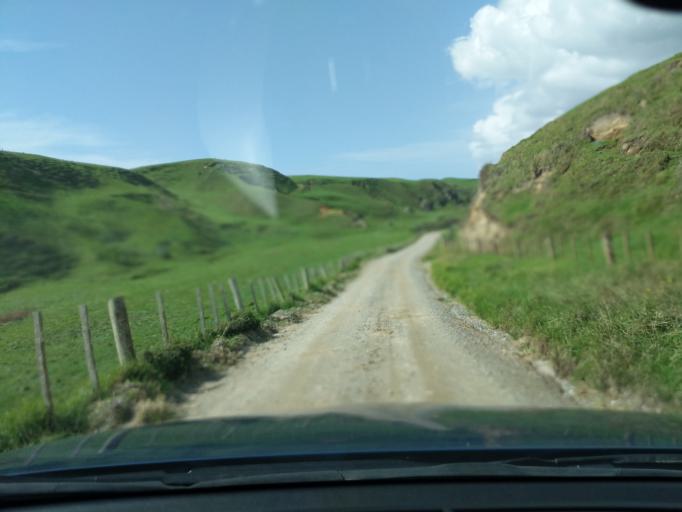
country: NZ
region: Tasman
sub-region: Tasman District
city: Takaka
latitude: -40.6536
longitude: 172.4183
